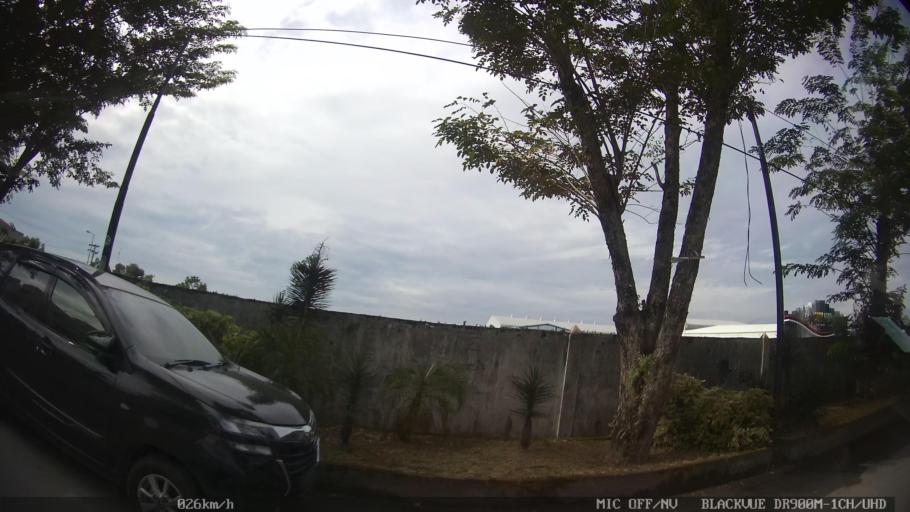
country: ID
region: North Sumatra
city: Sunggal
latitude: 3.6054
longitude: 98.6233
